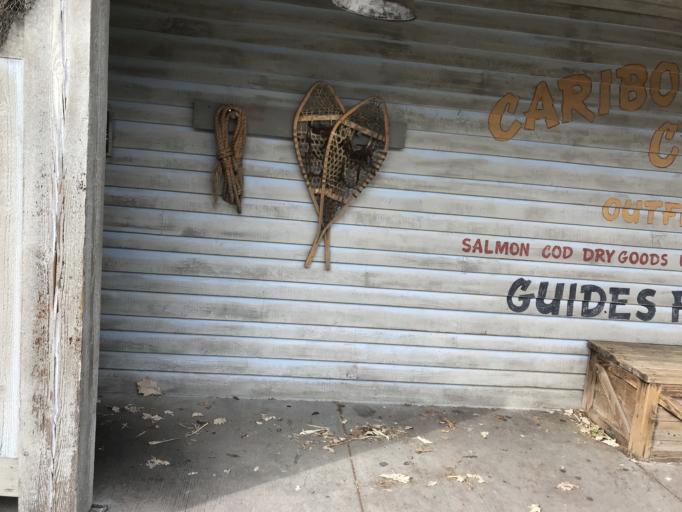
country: US
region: Kentucky
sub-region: Jefferson County
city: Audubon Park
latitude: 38.2039
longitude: -85.7035
